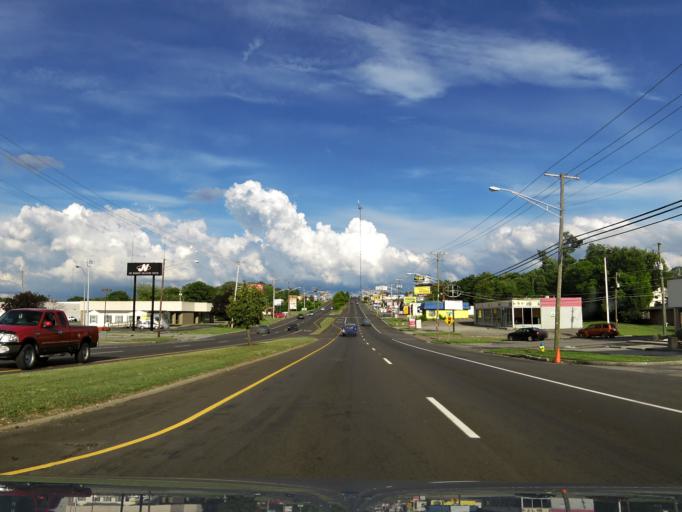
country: US
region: Tennessee
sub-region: Knox County
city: Knoxville
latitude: 36.0034
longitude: -83.9794
